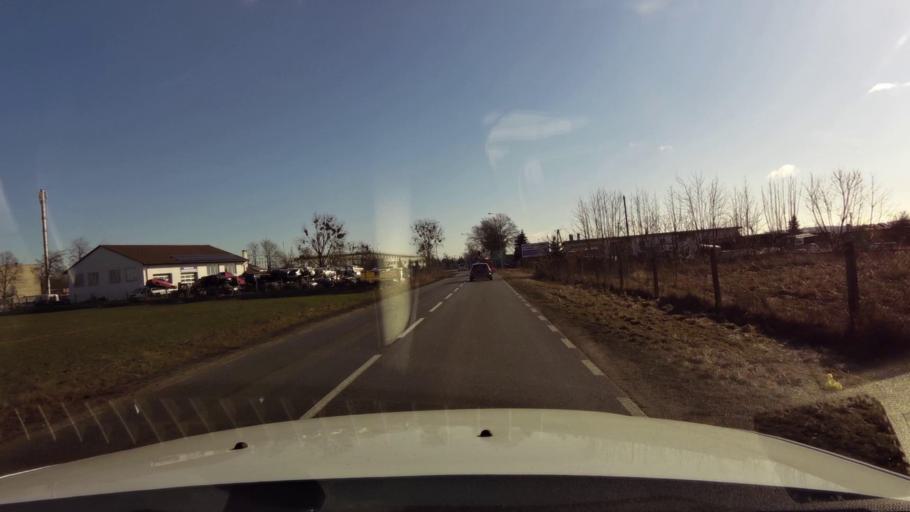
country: PL
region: West Pomeranian Voivodeship
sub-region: Powiat mysliborski
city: Barlinek
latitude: 52.9923
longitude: 15.1910
